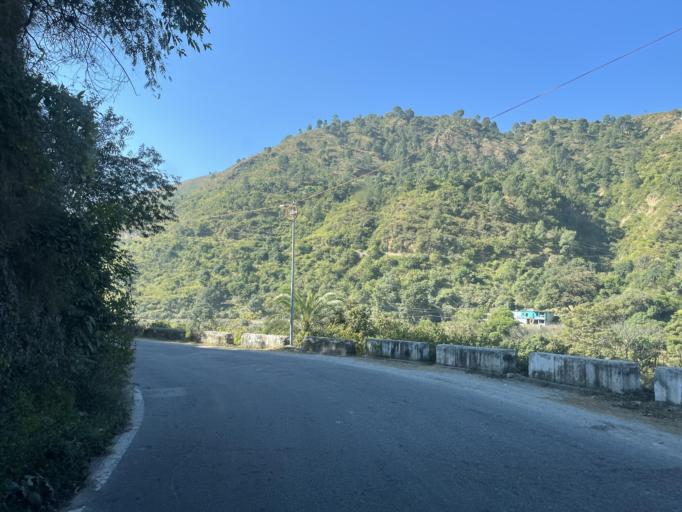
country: IN
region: Uttarakhand
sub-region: Naini Tal
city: Naini Tal
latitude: 29.5206
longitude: 79.4806
